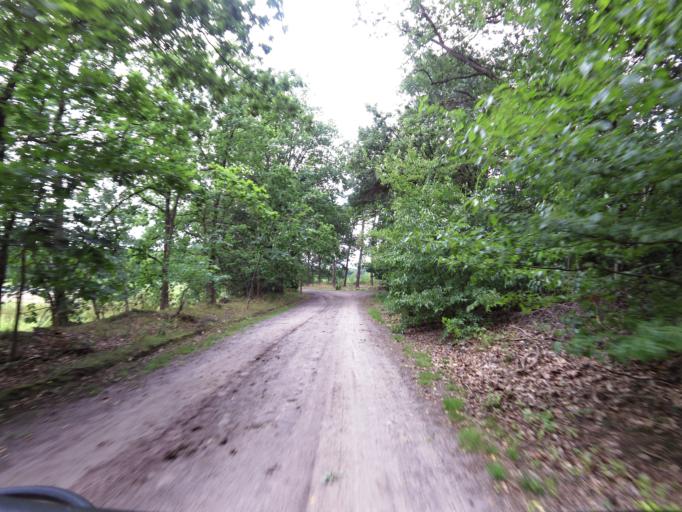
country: NL
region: North Brabant
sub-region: Gemeente Son en Breugel
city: Breugel
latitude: 51.5505
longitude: 5.5069
